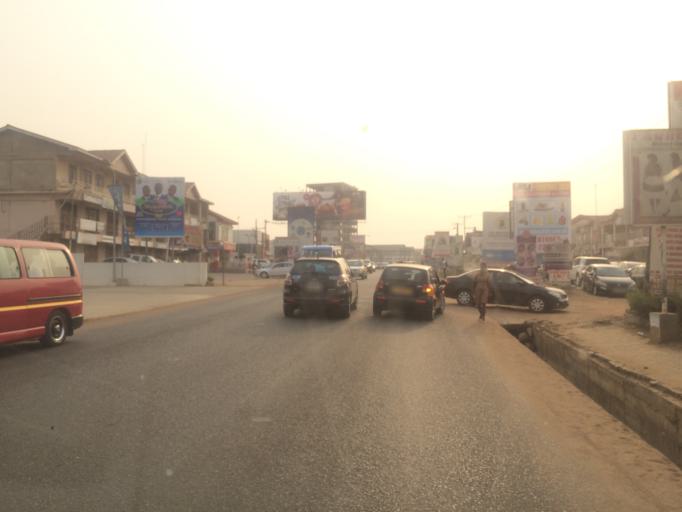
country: GH
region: Greater Accra
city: Nungua
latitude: 5.6251
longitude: -0.0771
